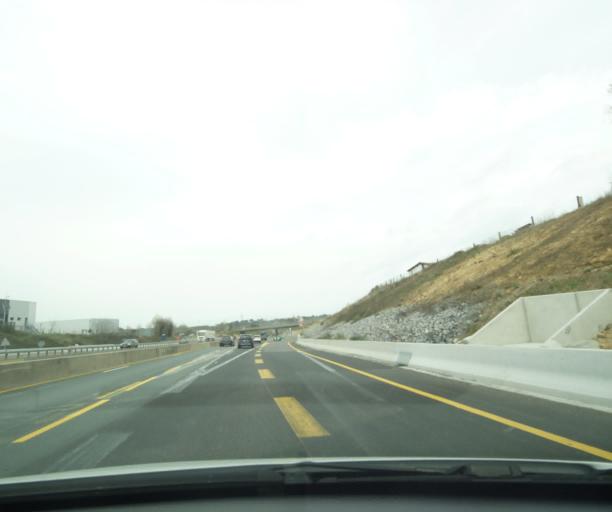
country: FR
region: Aquitaine
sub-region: Departement des Pyrenees-Atlantiques
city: Saint-Jean-de-Luz
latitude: 43.3990
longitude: -1.6364
